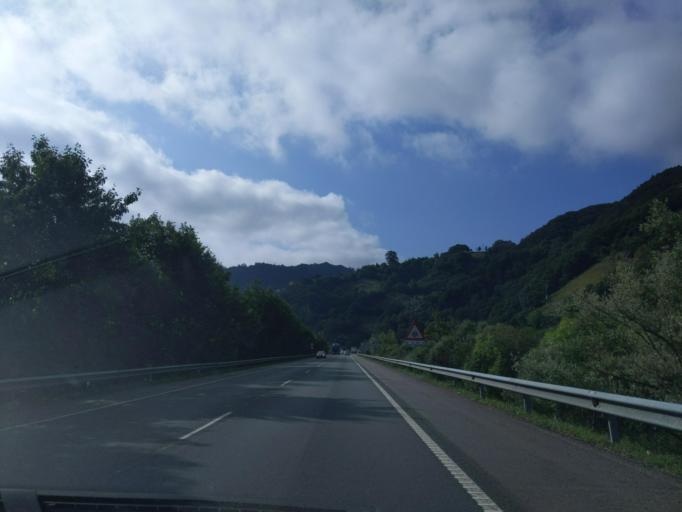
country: ES
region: Asturias
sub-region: Province of Asturias
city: El entrego
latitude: 43.2774
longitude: -5.6164
